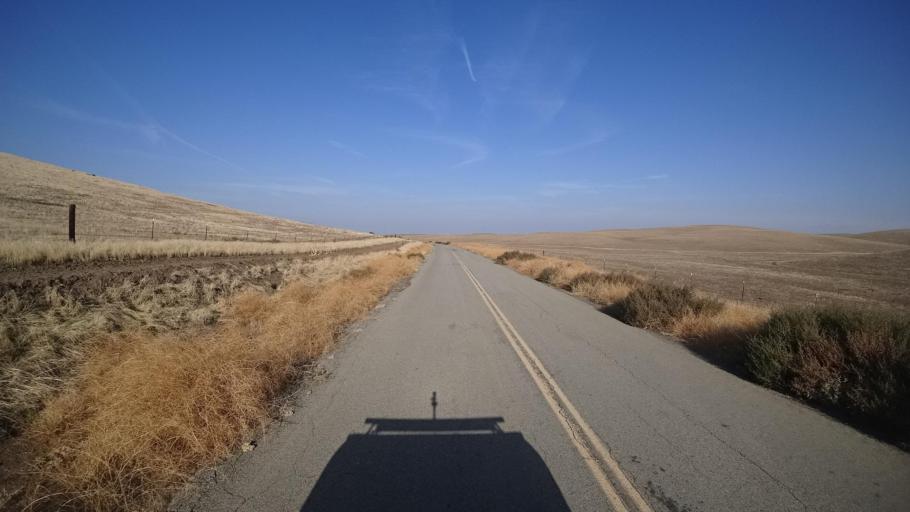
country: US
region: California
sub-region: Tulare County
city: Richgrove
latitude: 35.6344
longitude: -119.0355
